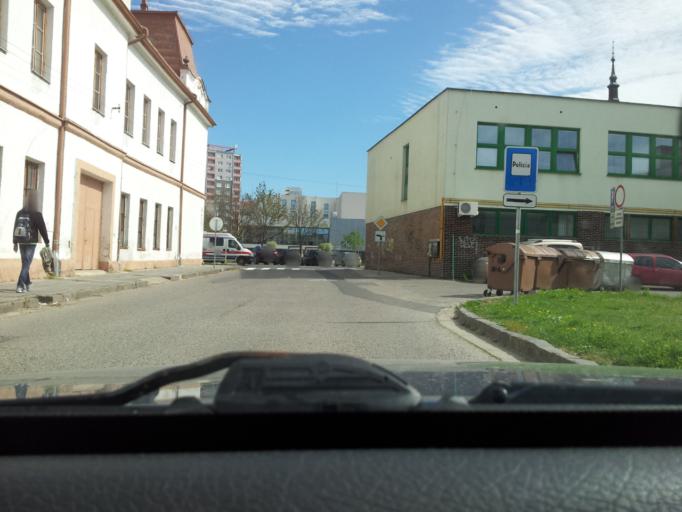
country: SK
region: Nitriansky
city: Levice
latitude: 48.2191
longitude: 18.6036
